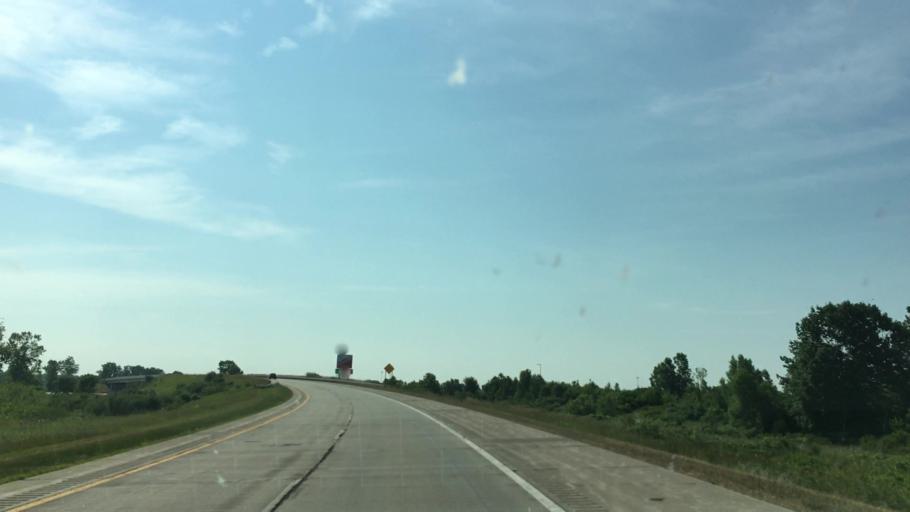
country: US
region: Michigan
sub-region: Clinton County
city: Wacousta
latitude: 42.7910
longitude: -84.6821
